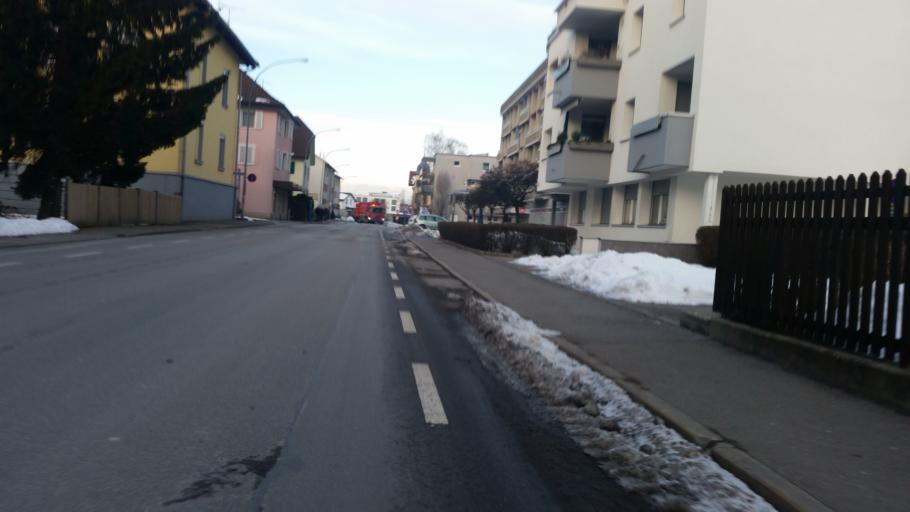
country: AT
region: Vorarlberg
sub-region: Politischer Bezirk Bregenz
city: Bregenz
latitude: 47.5028
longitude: 9.7289
